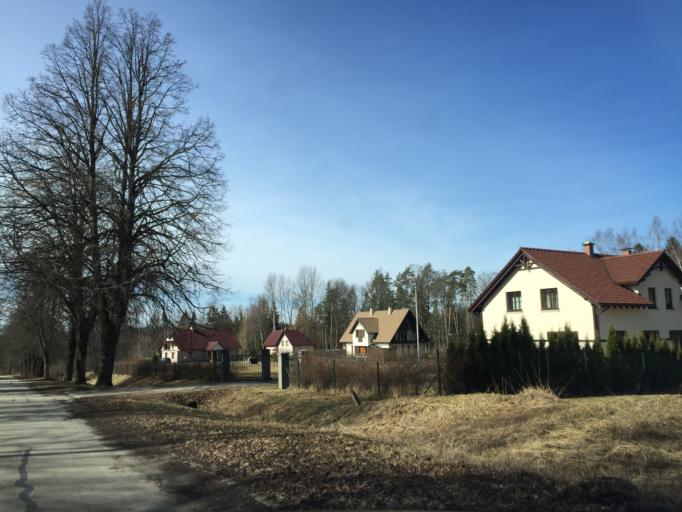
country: LV
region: Sigulda
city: Sigulda
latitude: 57.1383
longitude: 24.8190
